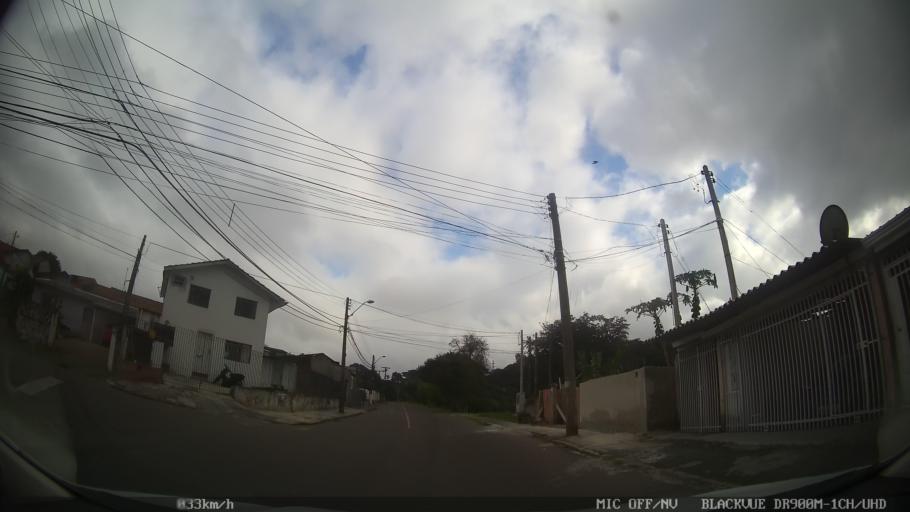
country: BR
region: Parana
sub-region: Curitiba
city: Curitiba
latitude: -25.3756
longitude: -49.2561
